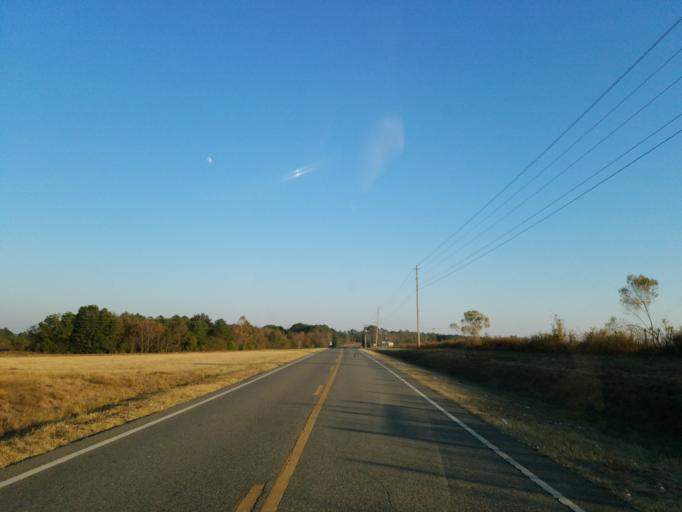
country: US
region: Georgia
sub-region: Crisp County
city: Cordele
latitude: 31.8715
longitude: -83.6624
